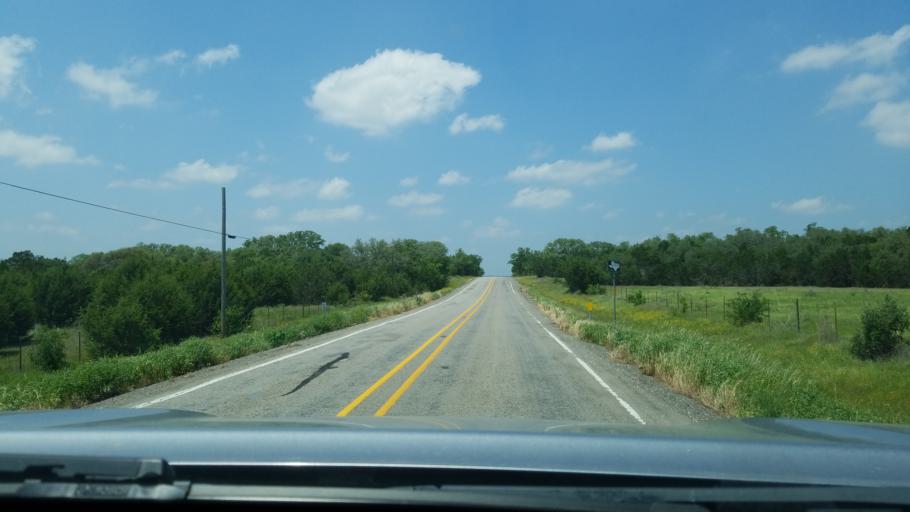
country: US
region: Texas
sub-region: Hays County
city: Woodcreek
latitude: 30.0524
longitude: -98.2032
